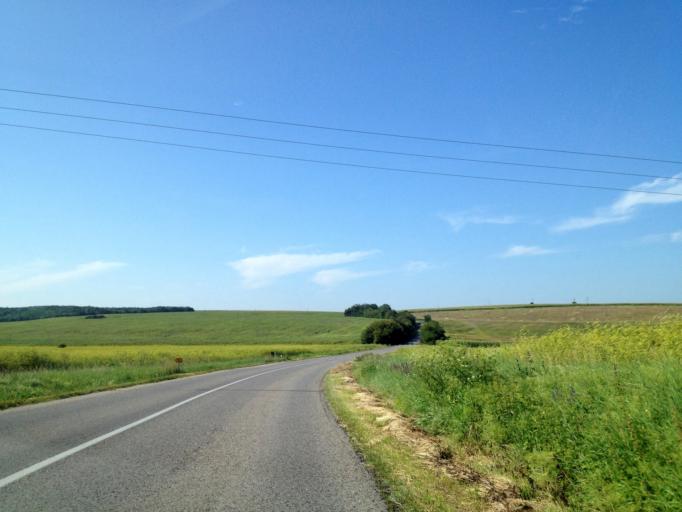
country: SK
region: Nitriansky
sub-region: Okres Komarno
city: Hurbanovo
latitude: 47.8827
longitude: 18.2900
